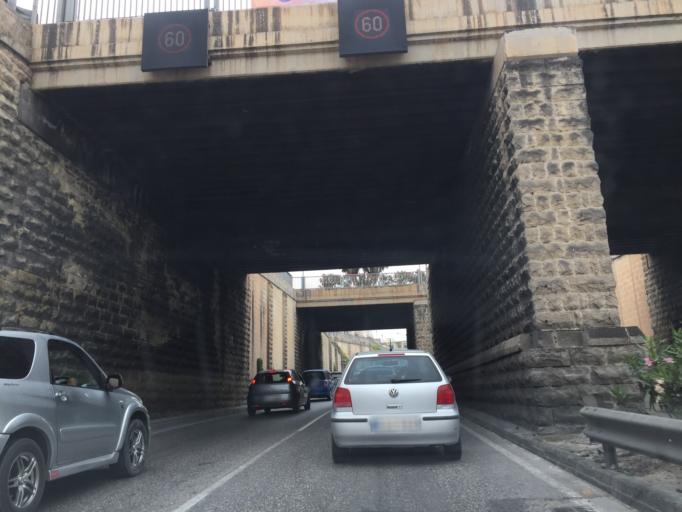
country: MT
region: L-Imsida
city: Imsida
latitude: 35.8930
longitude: 14.4830
